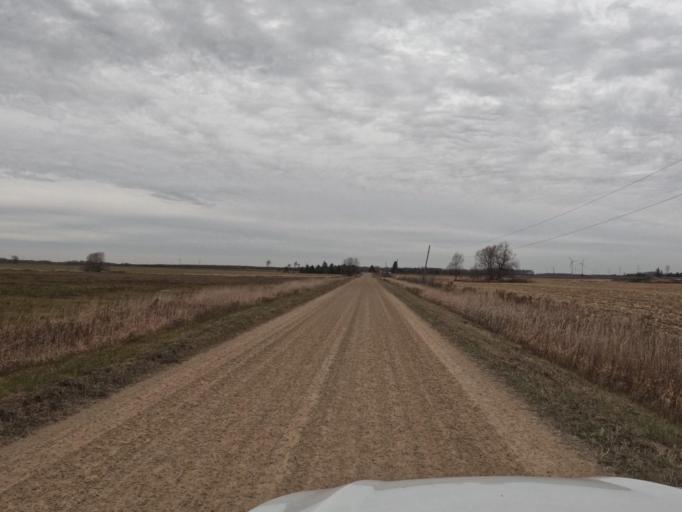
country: CA
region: Ontario
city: Shelburne
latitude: 44.0344
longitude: -80.3721
